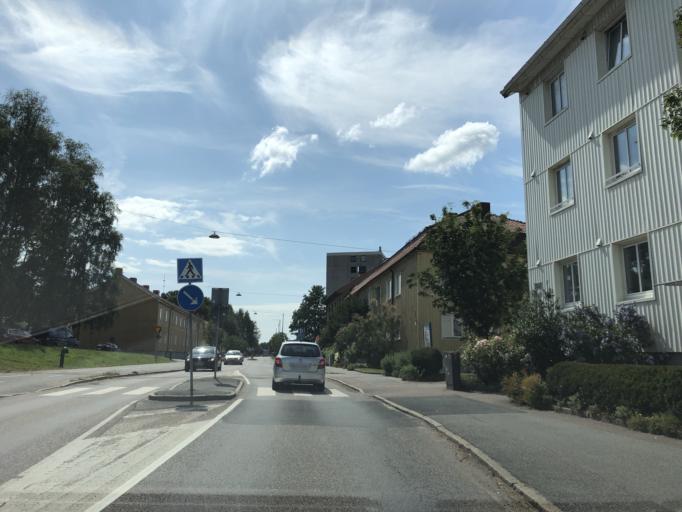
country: SE
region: Vaestra Goetaland
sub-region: Goteborg
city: Majorna
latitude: 57.7165
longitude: 11.9294
